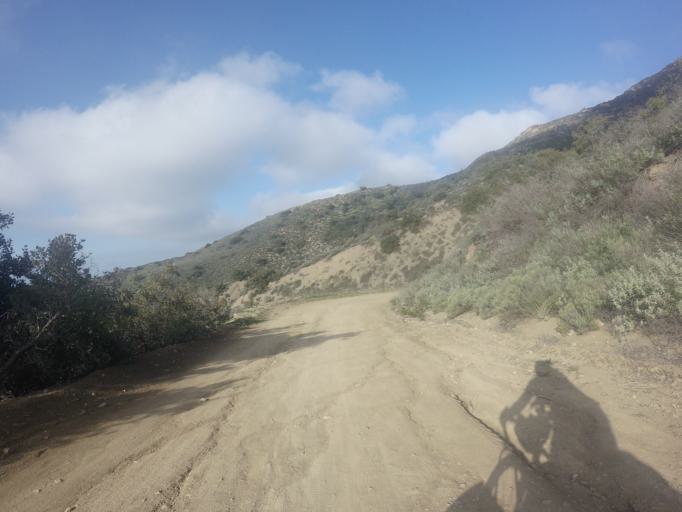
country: US
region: California
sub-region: Orange County
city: Foothill Ranch
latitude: 33.7970
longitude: -117.6608
